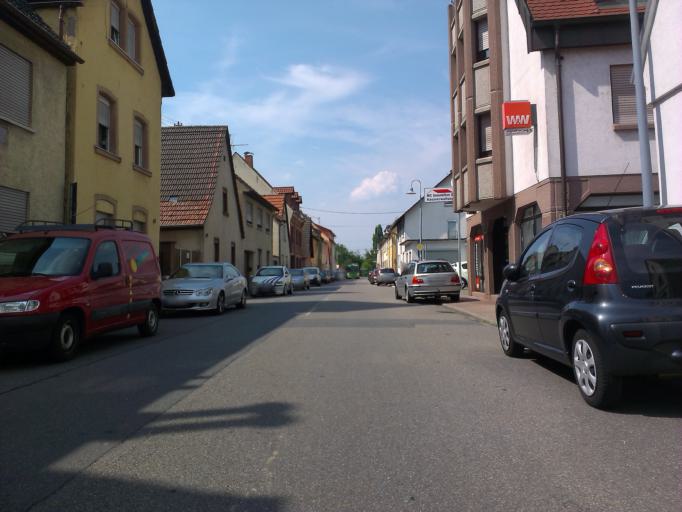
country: DE
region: Baden-Wuerttemberg
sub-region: Karlsruhe Region
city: Edingen-Neckarhausen
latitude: 49.4497
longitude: 8.6105
